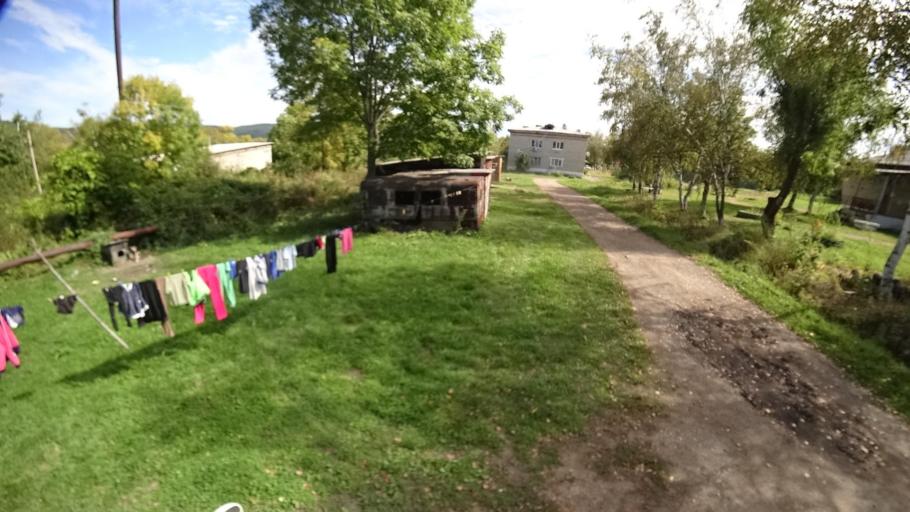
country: RU
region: Primorskiy
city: Yakovlevka
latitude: 44.4005
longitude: 133.5998
